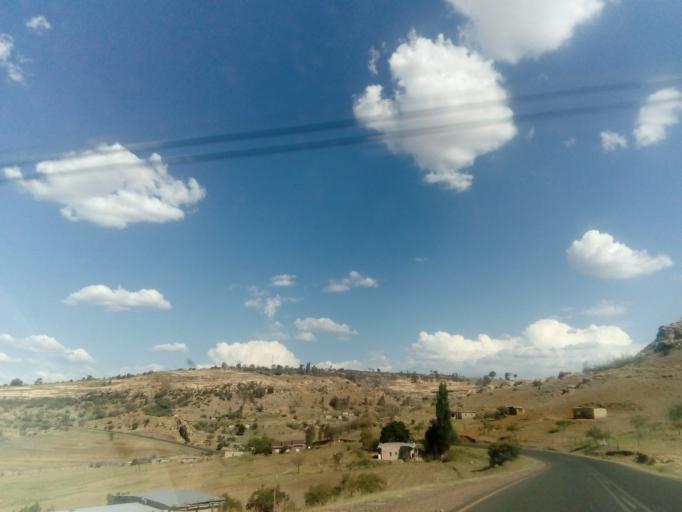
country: LS
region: Berea
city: Teyateyaneng
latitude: -29.1166
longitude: 27.8096
